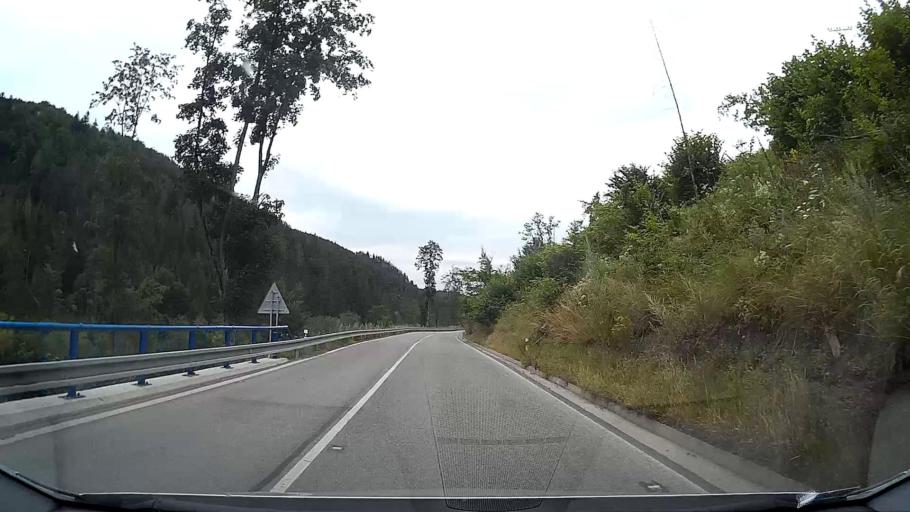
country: SK
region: Presovsky
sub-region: Okres Poprad
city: Poprad
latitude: 48.9438
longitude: 20.2883
